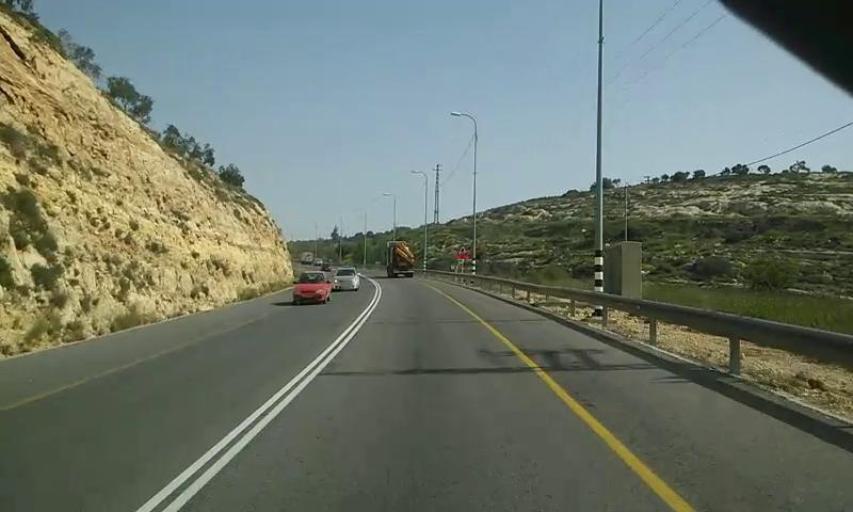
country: PS
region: West Bank
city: Yatma
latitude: 32.1116
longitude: 35.2573
